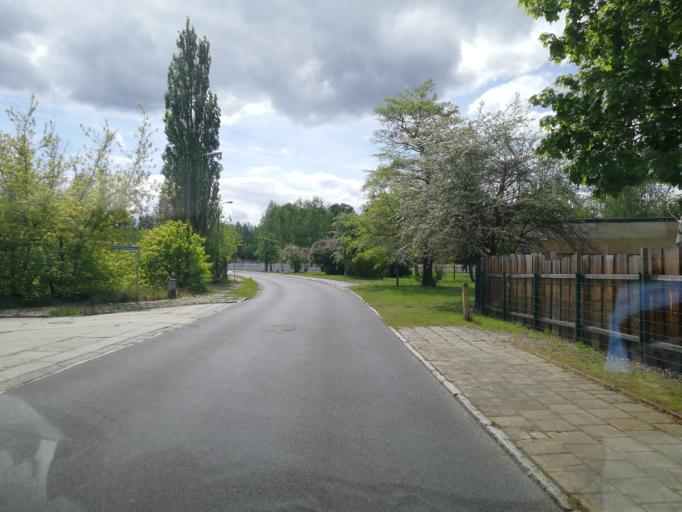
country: DE
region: Brandenburg
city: Lauchhammer
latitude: 51.5062
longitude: 13.7986
